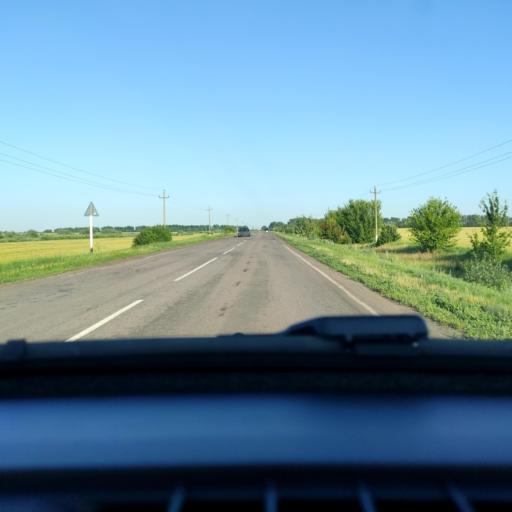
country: RU
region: Voronezj
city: Kashirskoye
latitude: 51.4957
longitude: 39.8376
